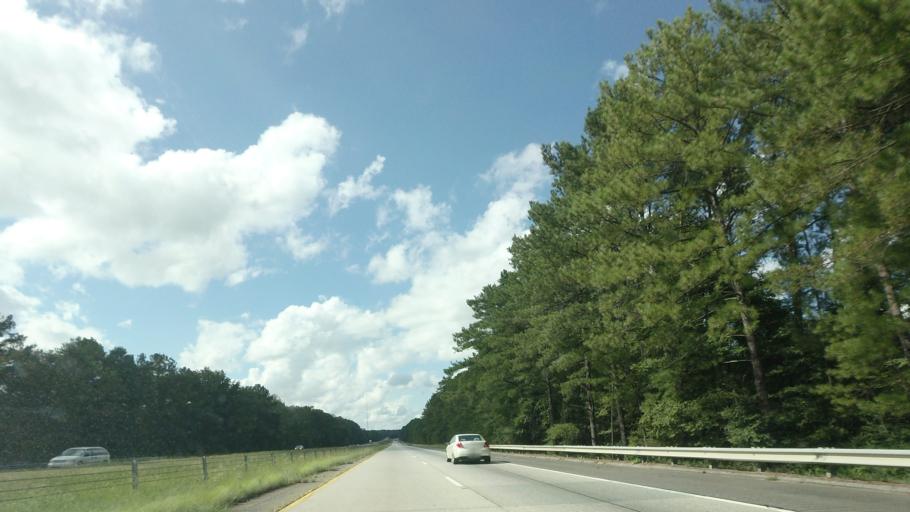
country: US
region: Georgia
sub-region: Bibb County
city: Macon
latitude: 32.7475
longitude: -83.5474
